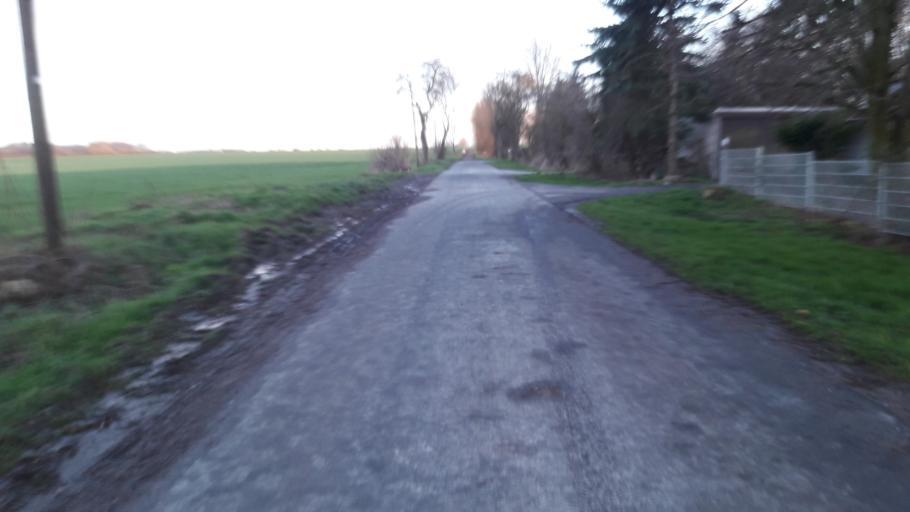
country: DE
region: North Rhine-Westphalia
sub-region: Regierungsbezirk Detmold
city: Paderborn
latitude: 51.6933
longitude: 8.7735
